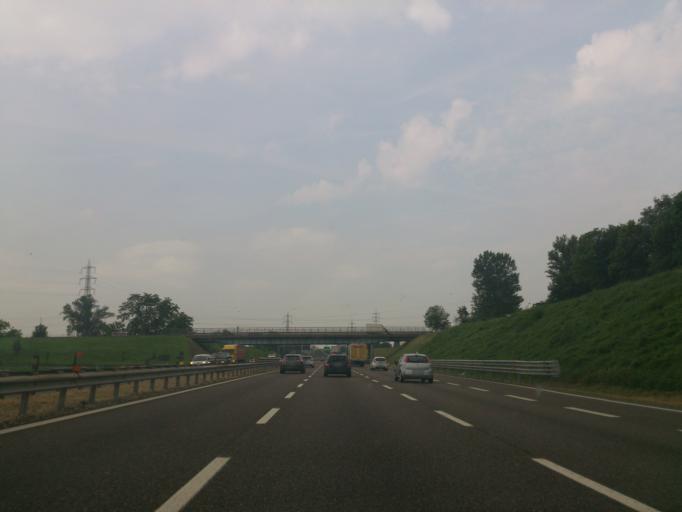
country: IT
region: Lombardy
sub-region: Provincia di Monza e Brianza
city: Brugherio
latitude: 45.5386
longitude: 9.3071
